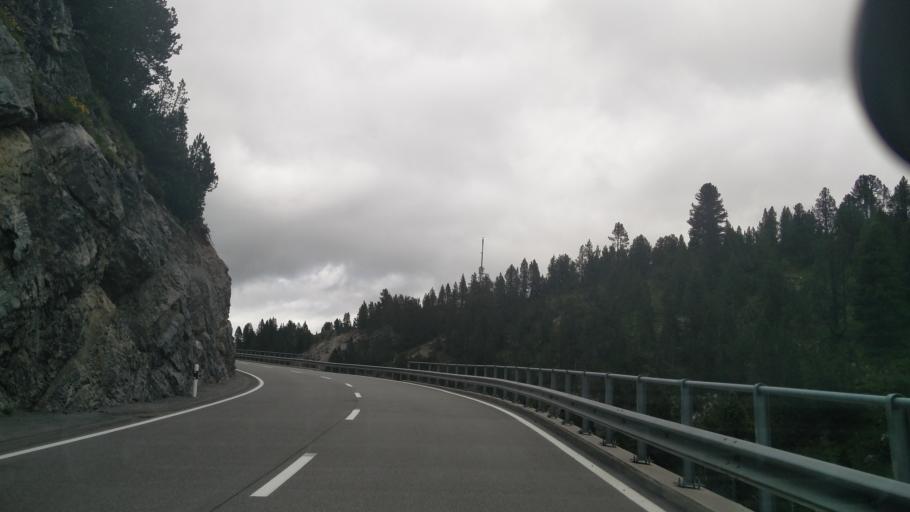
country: IT
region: Lombardy
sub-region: Provincia di Sondrio
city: Isolaccia
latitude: 46.6413
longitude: 10.2876
